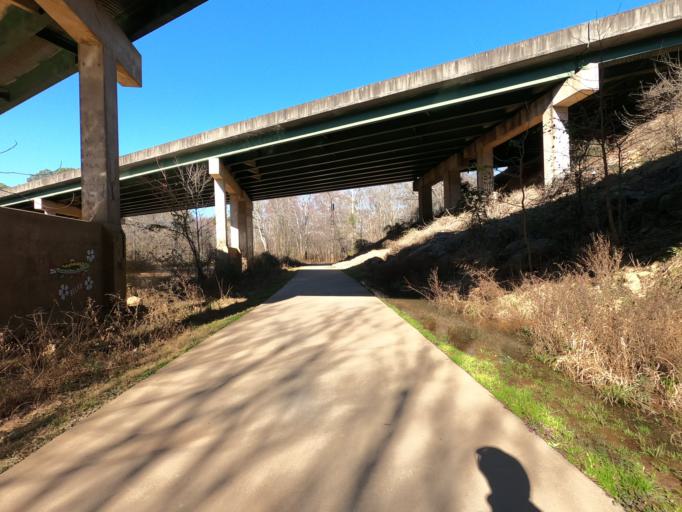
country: US
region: Georgia
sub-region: Clarke County
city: Athens
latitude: 33.9767
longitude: -83.3815
